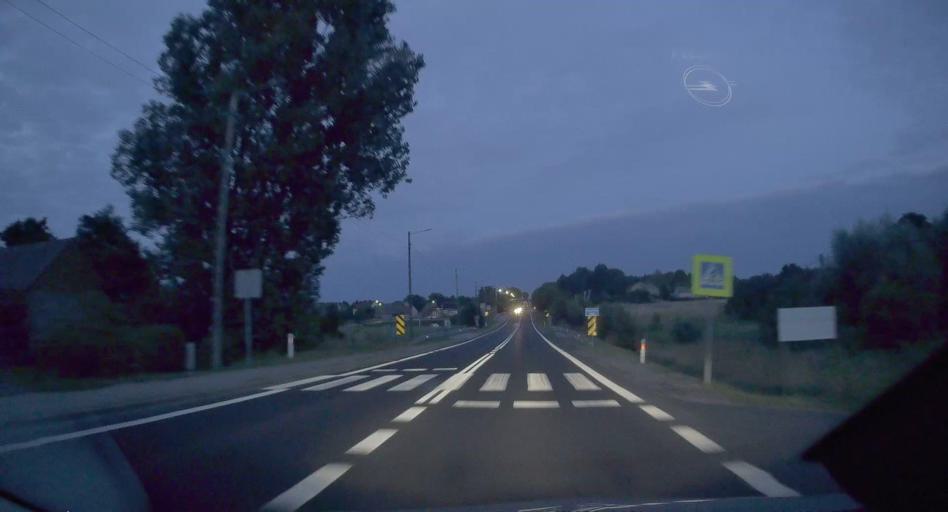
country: PL
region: Silesian Voivodeship
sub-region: Powiat klobucki
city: Lobodno
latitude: 50.8844
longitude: 18.9838
